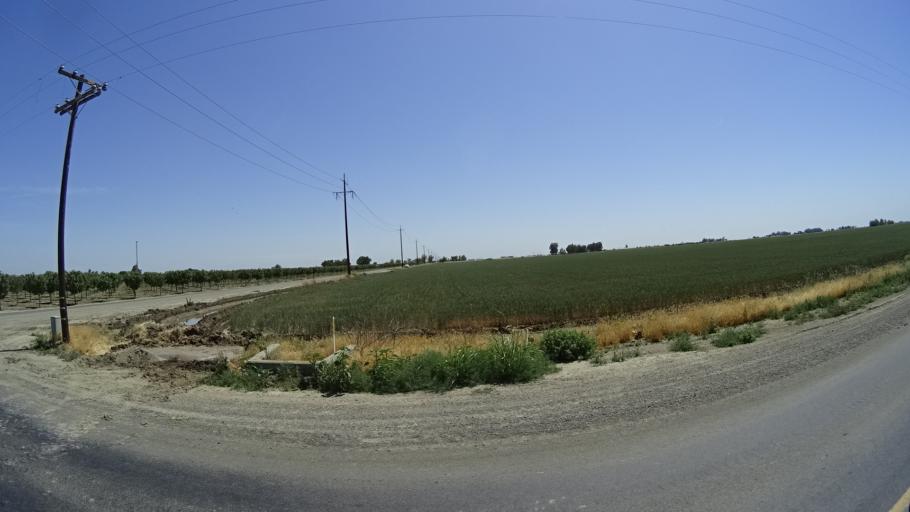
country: US
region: California
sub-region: Kings County
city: Stratford
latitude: 36.2258
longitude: -119.7982
